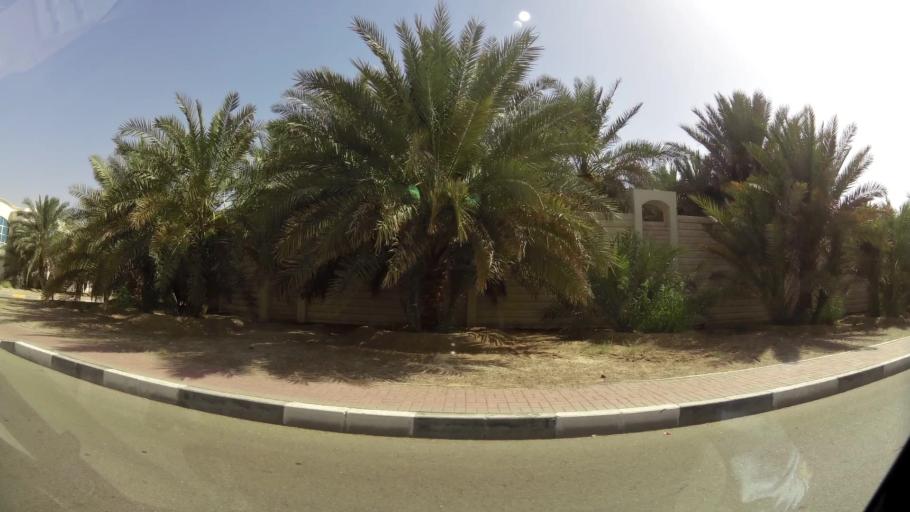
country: OM
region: Al Buraimi
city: Al Buraymi
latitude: 24.3073
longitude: 55.7968
